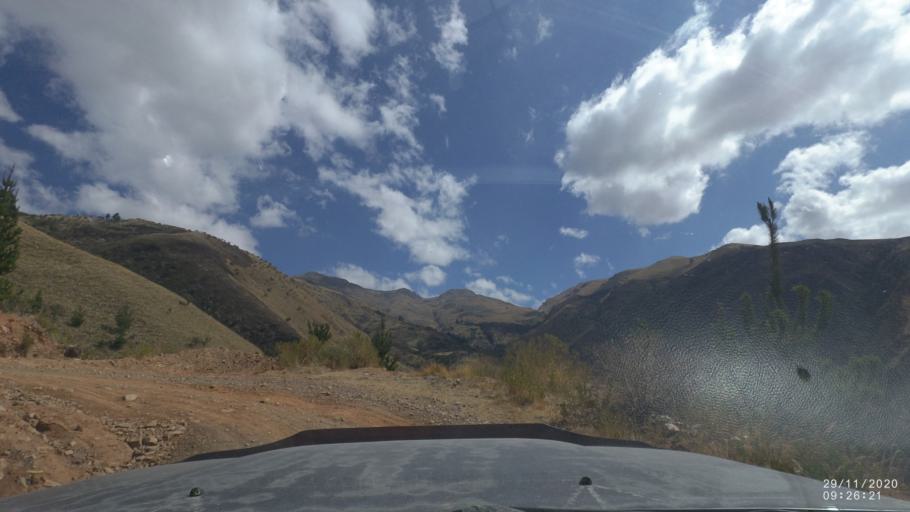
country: BO
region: Cochabamba
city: Cochabamba
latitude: -17.3186
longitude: -66.1849
